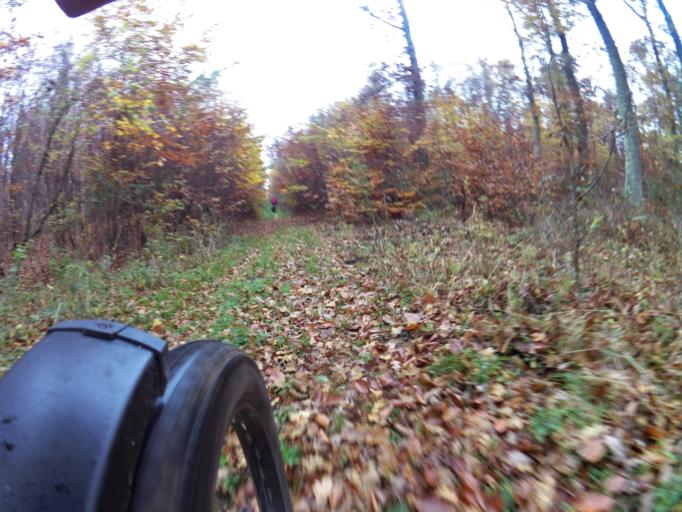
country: PL
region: Pomeranian Voivodeship
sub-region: Powiat pucki
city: Krokowa
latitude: 54.7307
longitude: 18.1322
